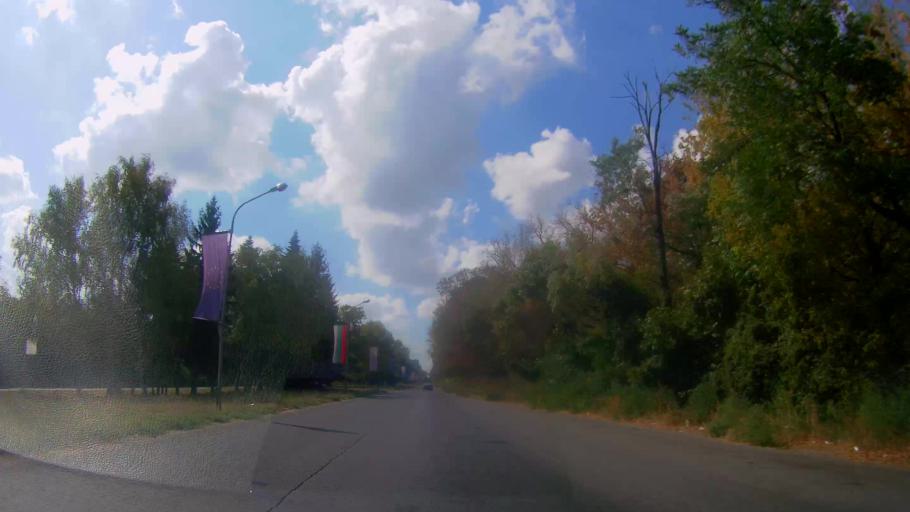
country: RO
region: Giurgiu
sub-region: Comuna Slobozia
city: Slobozia
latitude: 43.8038
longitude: 25.9208
